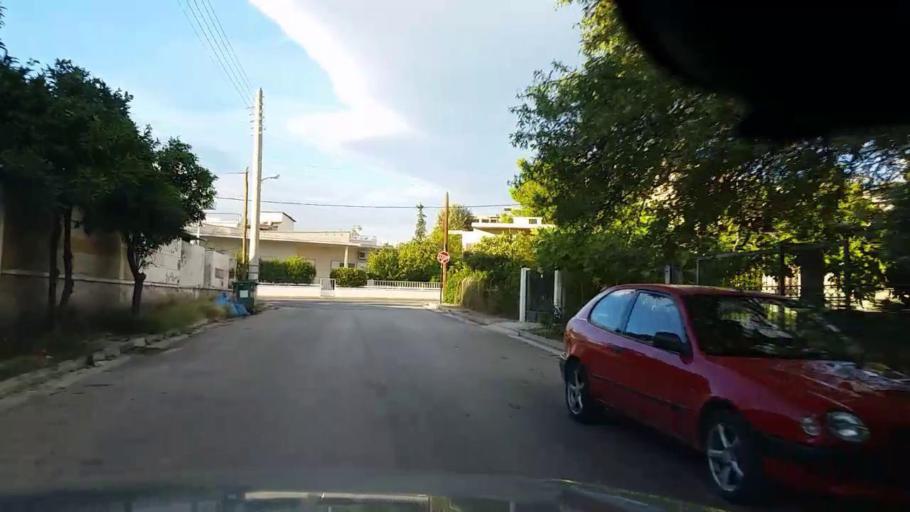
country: GR
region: Attica
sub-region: Nomarchia Anatolikis Attikis
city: Spata
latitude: 37.9636
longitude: 23.9063
